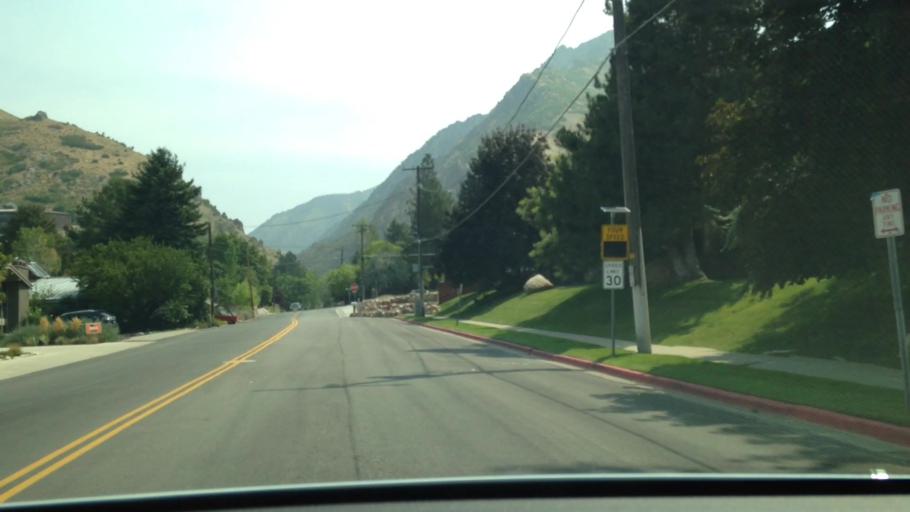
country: US
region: Utah
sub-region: Salt Lake County
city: Mount Olympus
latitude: 40.6891
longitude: -111.7927
